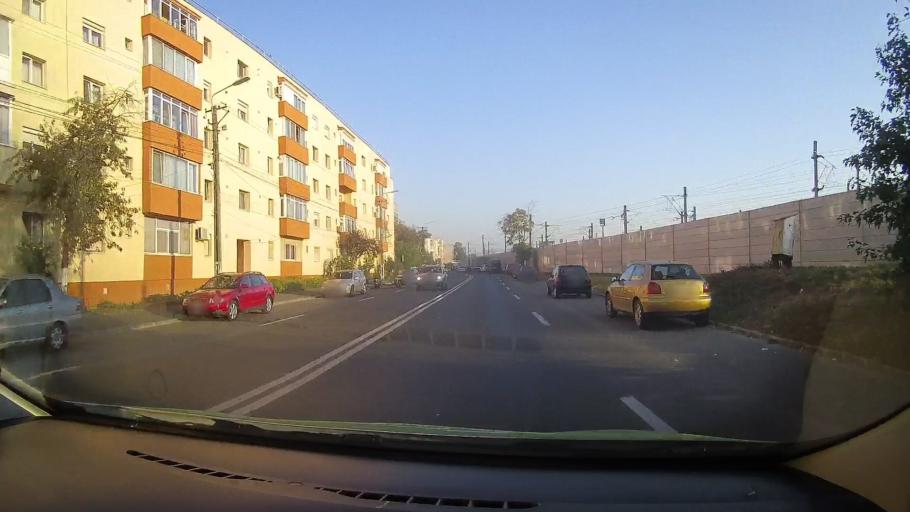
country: RO
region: Arad
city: Arad
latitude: 46.1959
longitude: 21.3206
